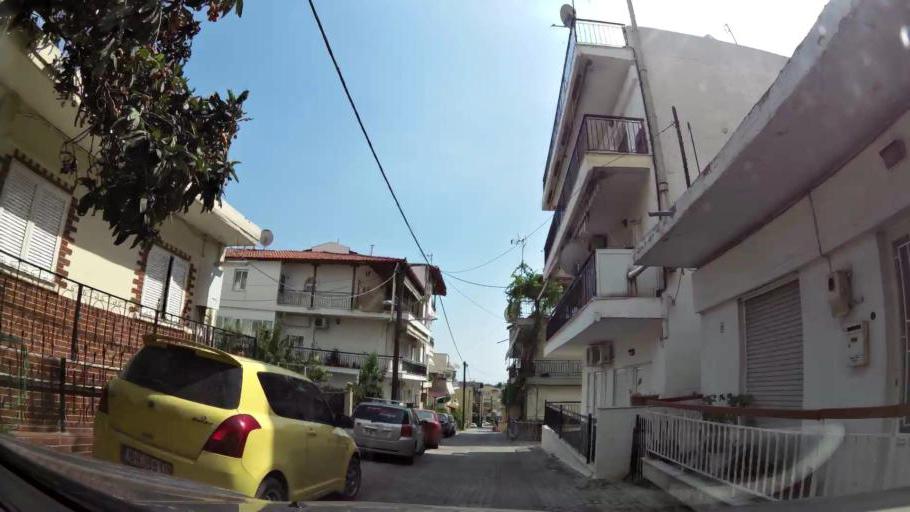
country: GR
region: Central Macedonia
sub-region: Nomos Thessalonikis
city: Stavroupoli
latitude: 40.6698
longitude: 22.9429
